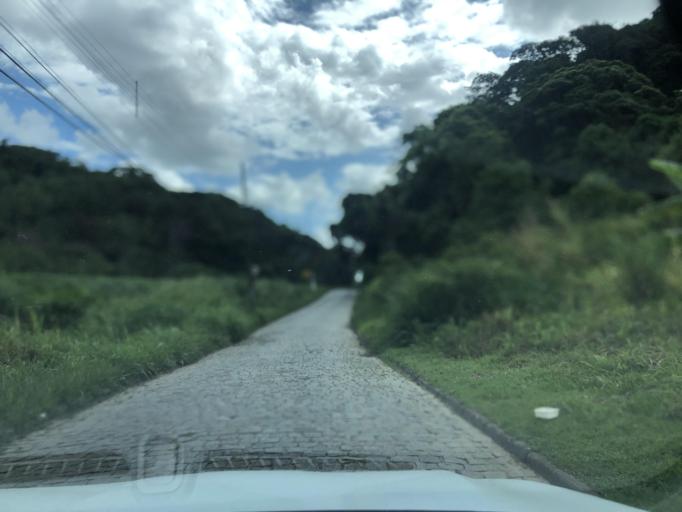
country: BR
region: Santa Catarina
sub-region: Sao Francisco Do Sul
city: Sao Francisco do Sul
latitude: -26.2342
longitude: -48.6270
